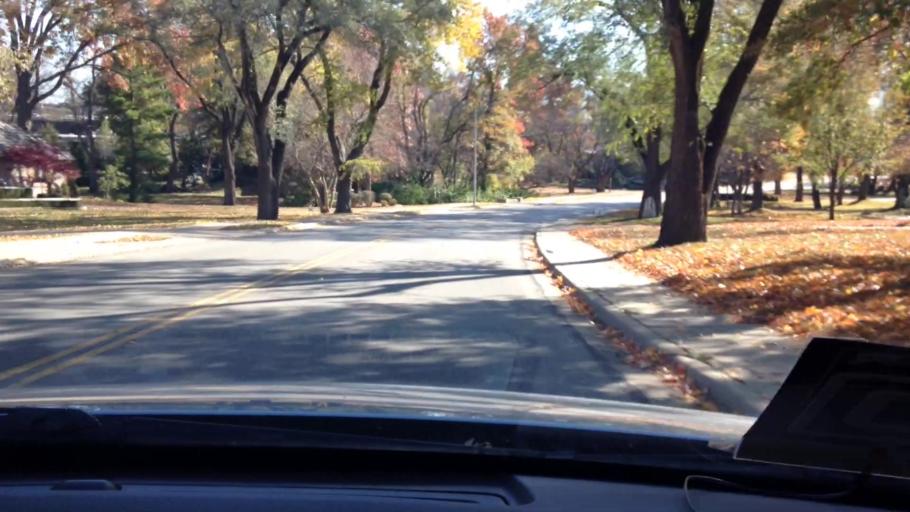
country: US
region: Kansas
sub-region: Johnson County
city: Prairie Village
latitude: 38.9775
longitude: -94.6392
